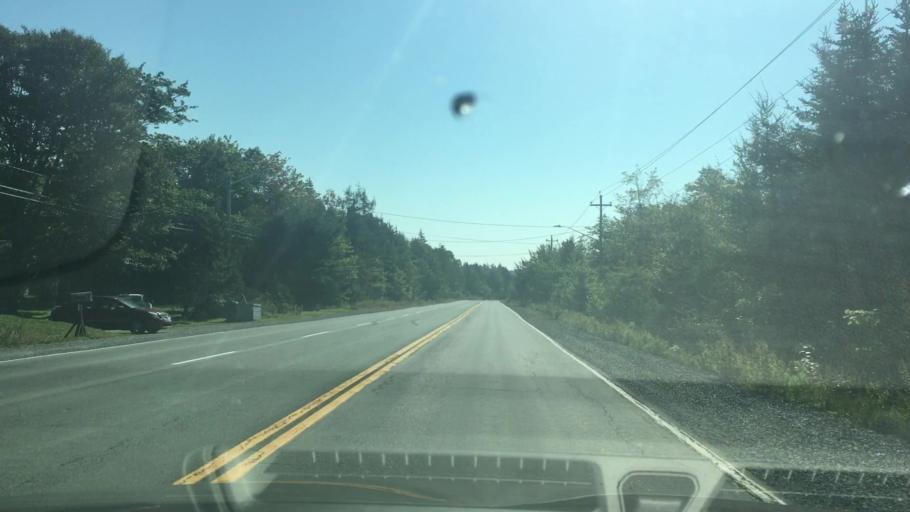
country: CA
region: Nova Scotia
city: Cole Harbour
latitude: 44.7787
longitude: -63.0776
